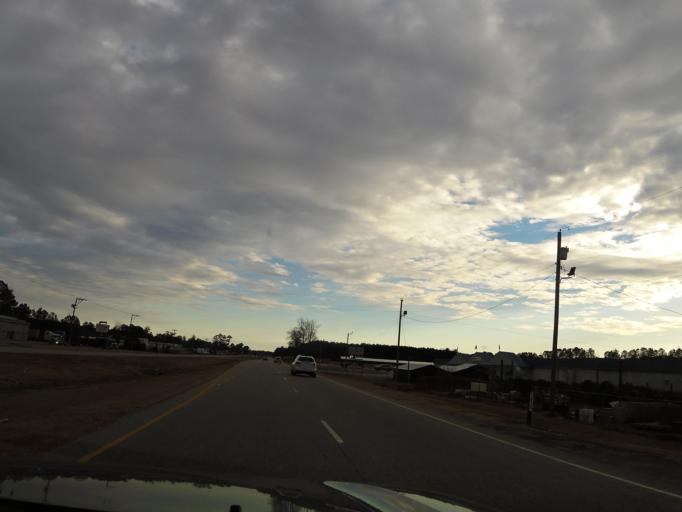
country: US
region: North Carolina
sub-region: Nash County
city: Sharpsburg
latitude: 35.9006
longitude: -77.8262
